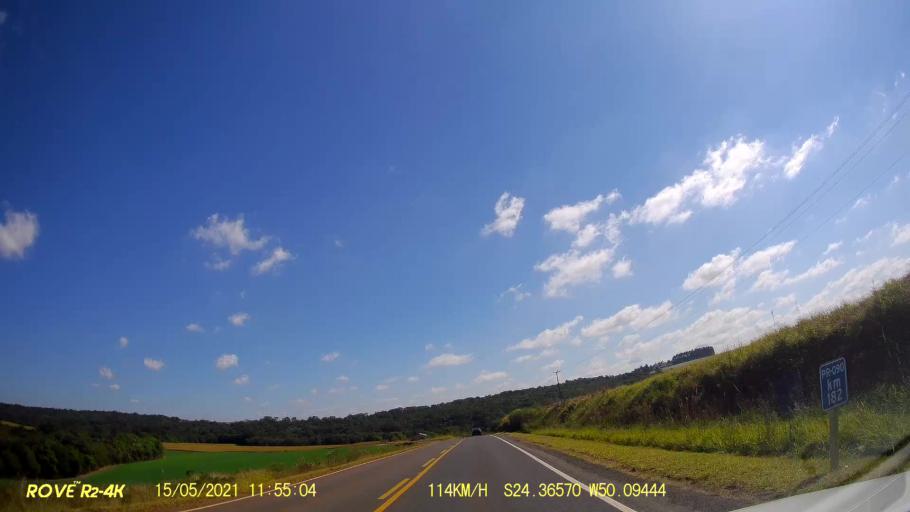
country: BR
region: Parana
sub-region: Pirai Do Sul
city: Pirai do Sul
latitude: -24.3658
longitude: -50.0937
